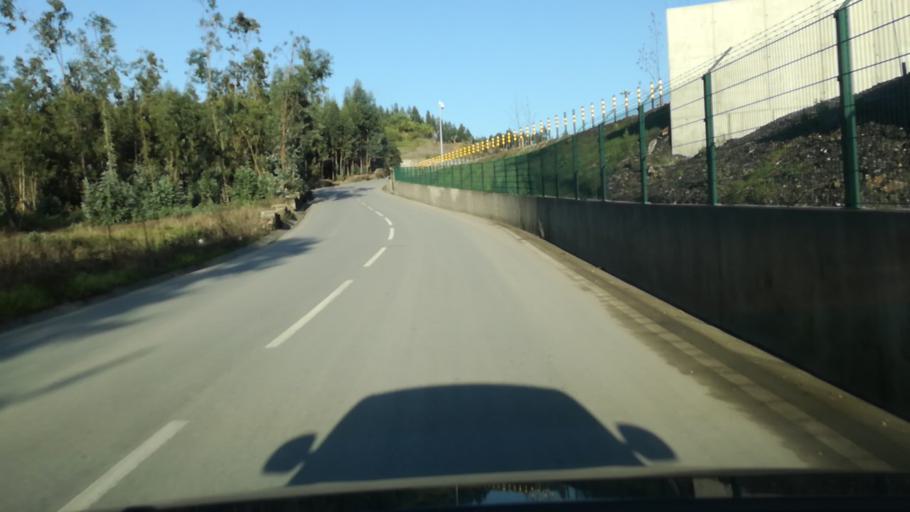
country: PT
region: Braga
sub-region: Vila Nova de Famalicao
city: Ferreiros
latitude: 41.3587
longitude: -8.5404
